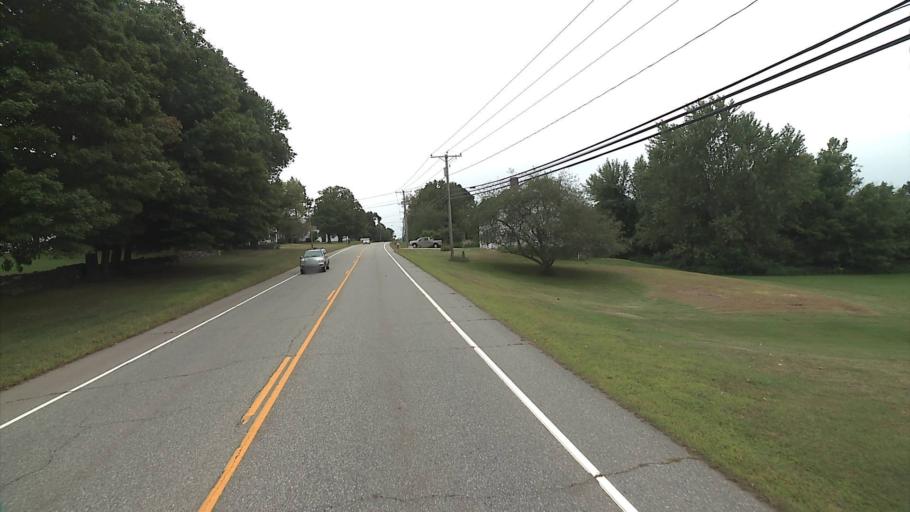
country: US
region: Connecticut
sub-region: Tolland County
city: Hebron
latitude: 41.6817
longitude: -72.4145
